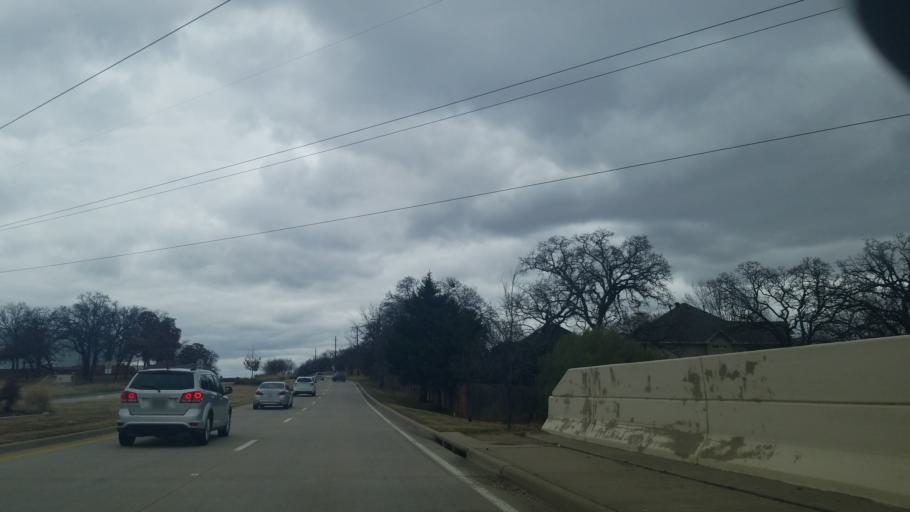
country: US
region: Texas
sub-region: Denton County
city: Copper Canyon
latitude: 33.0878
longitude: -97.0783
